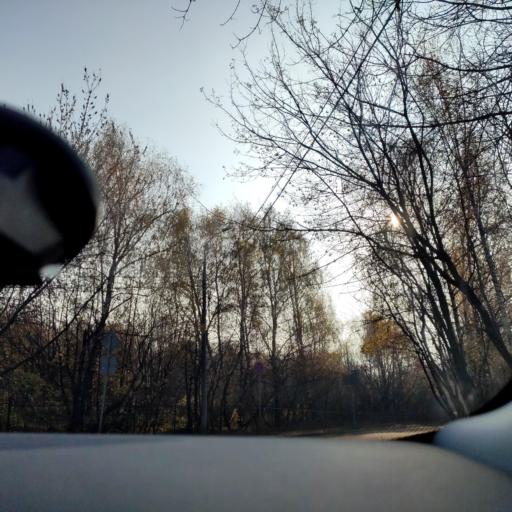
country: RU
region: Moscow
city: Kuz'minki
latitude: 55.6725
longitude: 37.8074
